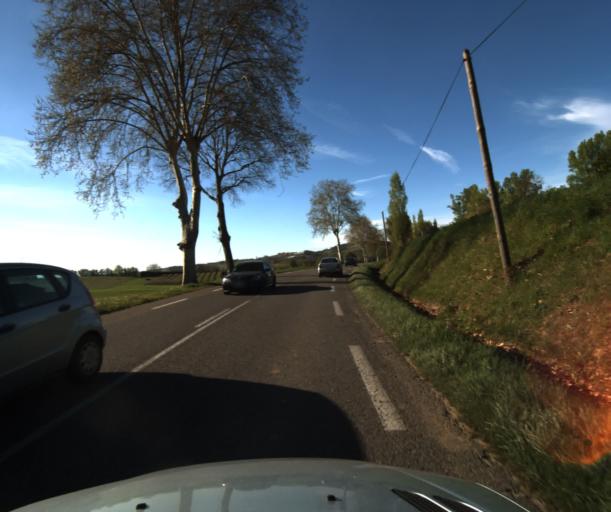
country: FR
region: Midi-Pyrenees
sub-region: Departement du Tarn-et-Garonne
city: Lafrancaise
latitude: 44.1335
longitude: 1.2211
